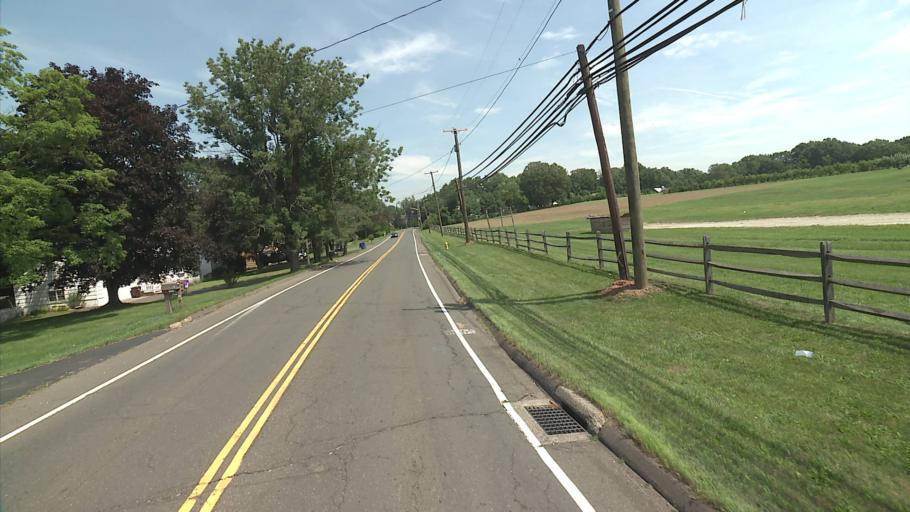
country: US
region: Connecticut
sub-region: New Haven County
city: North Branford
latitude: 41.3085
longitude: -72.7713
